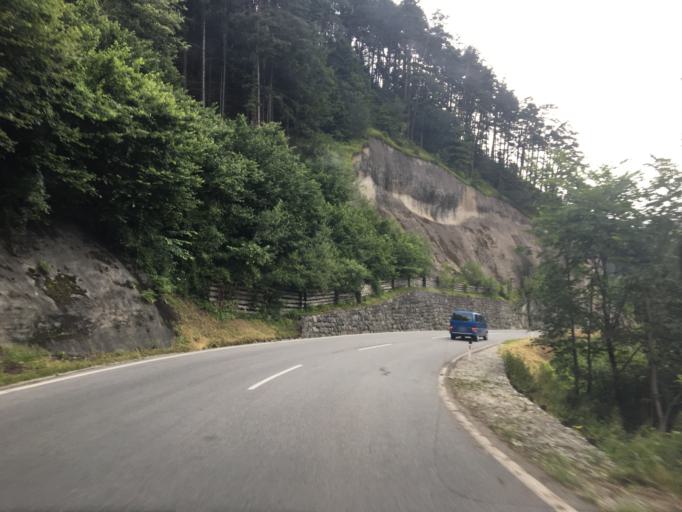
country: AT
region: Tyrol
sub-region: Politischer Bezirk Innsbruck Land
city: Patsch
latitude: 47.2095
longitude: 11.3969
